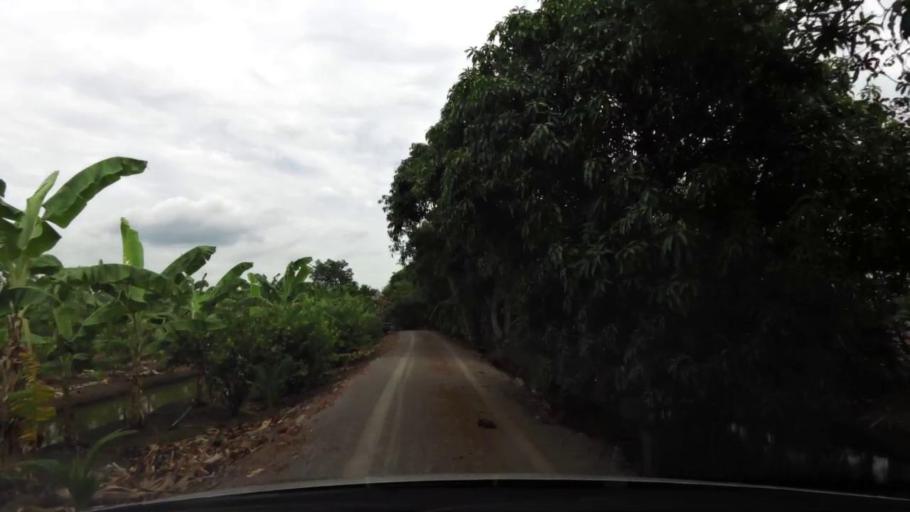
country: TH
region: Ratchaburi
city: Damnoen Saduak
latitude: 13.5535
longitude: 99.9757
